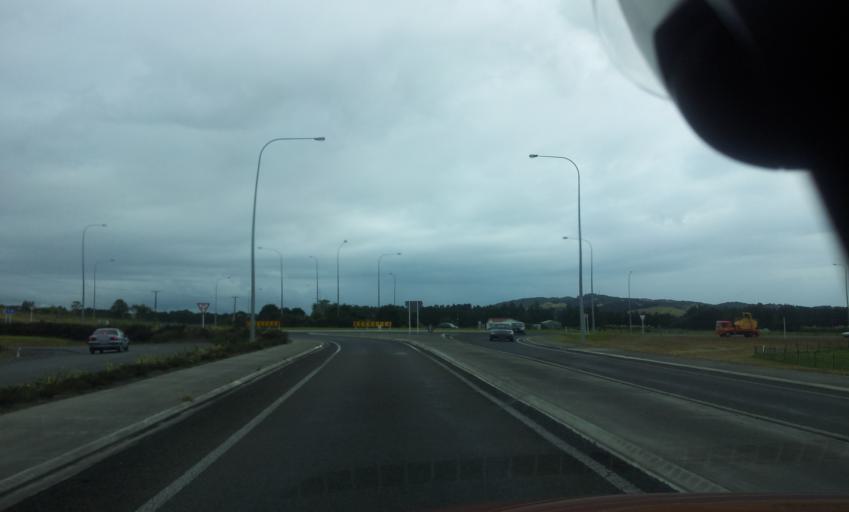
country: NZ
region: Northland
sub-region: Whangarei
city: Ruakaka
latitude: -35.8924
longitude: 174.4340
